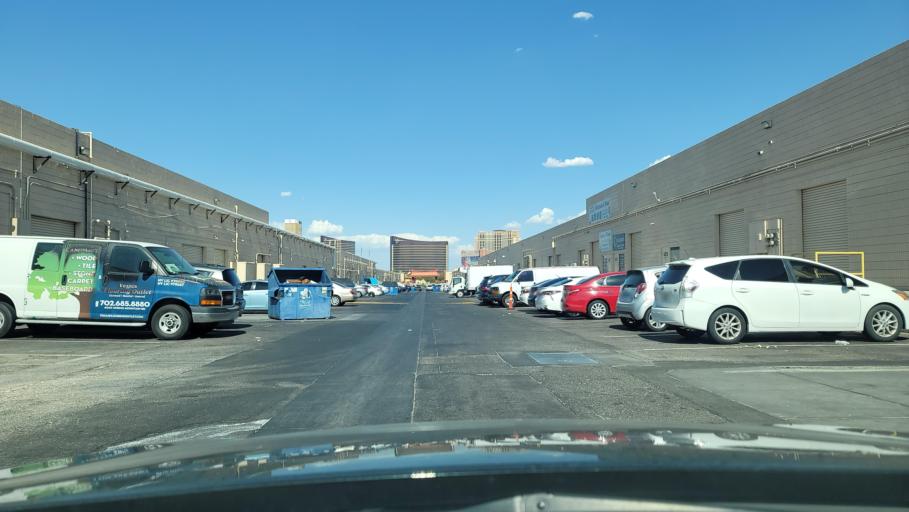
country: US
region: Nevada
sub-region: Clark County
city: Spring Valley
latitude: 36.1258
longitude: -115.1939
